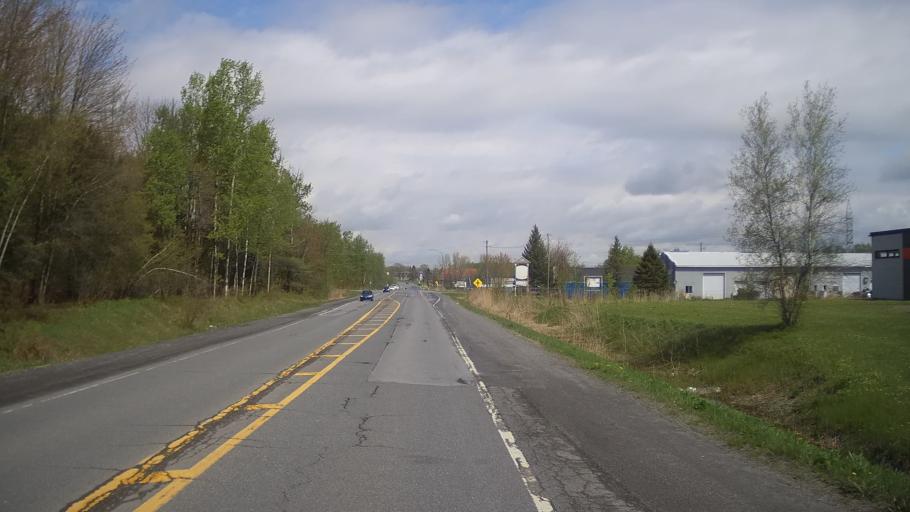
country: CA
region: Quebec
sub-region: Monteregie
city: Cowansville
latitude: 45.2022
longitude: -72.7651
